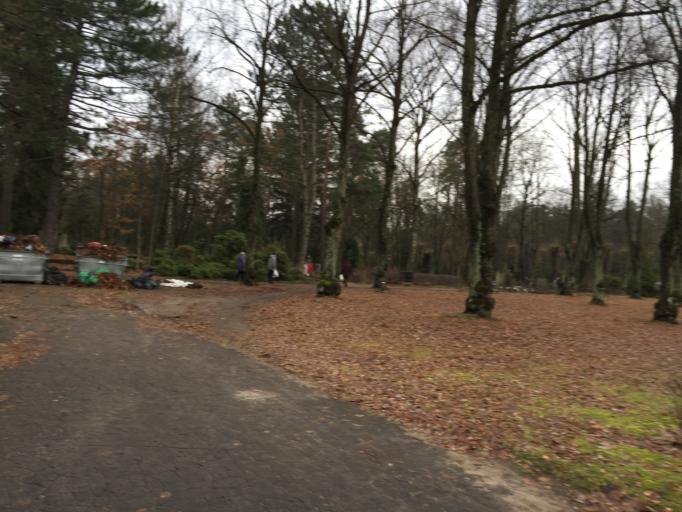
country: LV
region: Riga
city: Jaunciems
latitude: 56.9881
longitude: 24.1466
